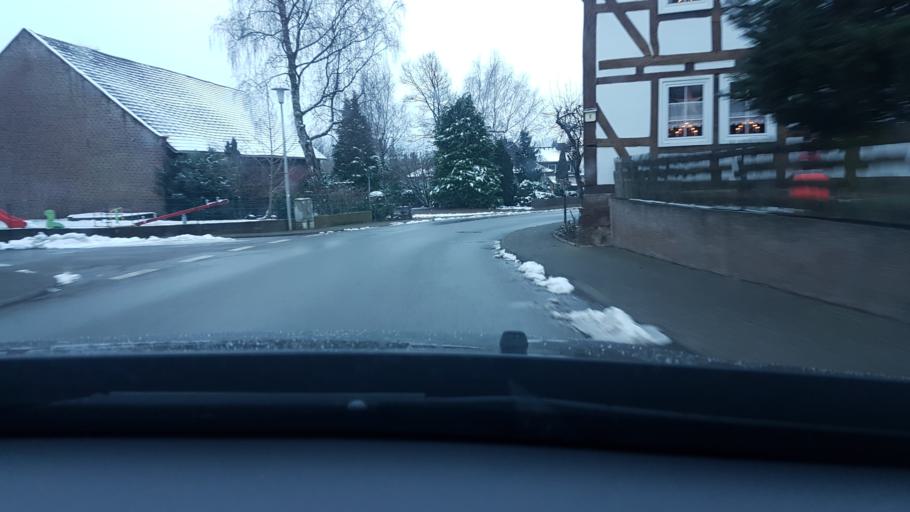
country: DE
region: North Rhine-Westphalia
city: Marsberg
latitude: 51.3841
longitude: 8.8927
